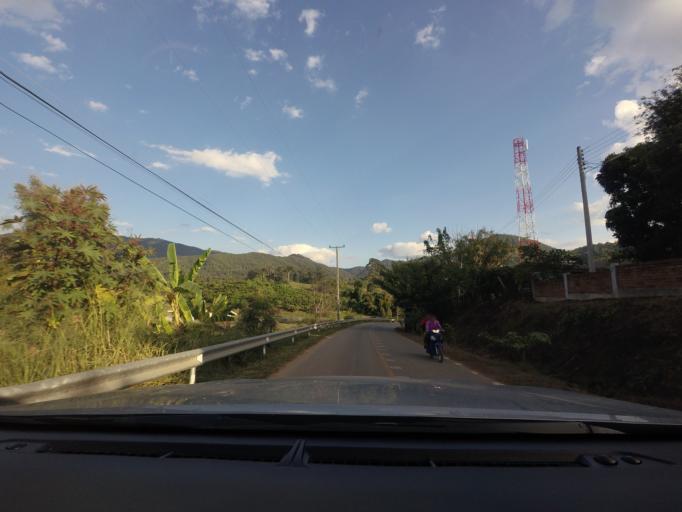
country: TH
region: Chiang Mai
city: Phrao
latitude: 19.5136
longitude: 99.1723
